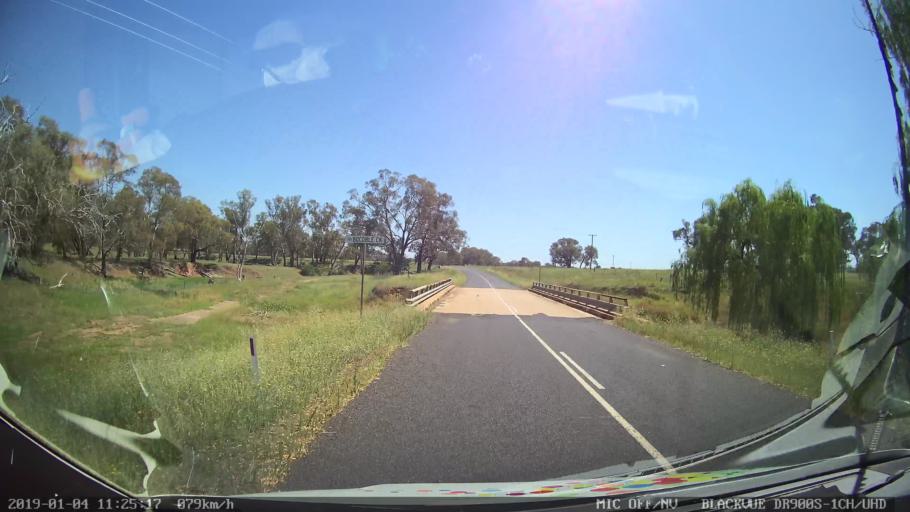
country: AU
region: New South Wales
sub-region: Cabonne
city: Molong
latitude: -33.1267
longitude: 148.7523
